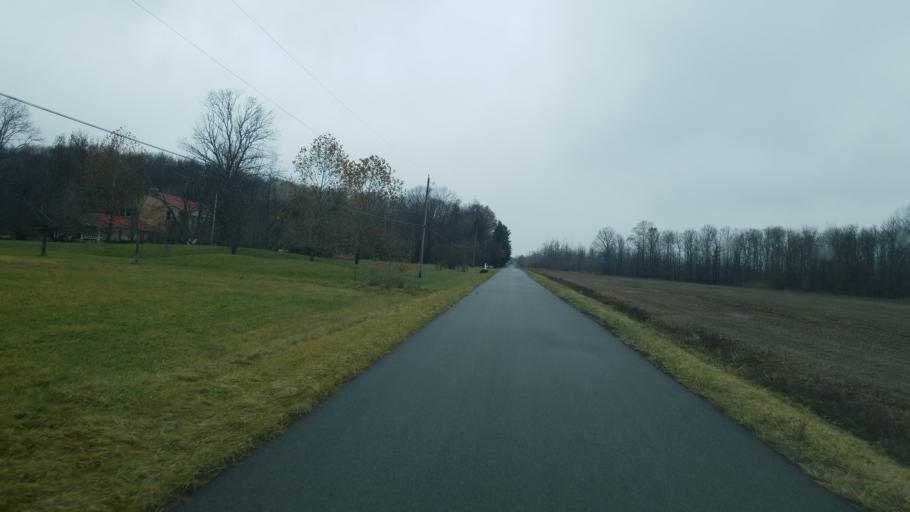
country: US
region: Ohio
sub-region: Ashtabula County
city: Andover
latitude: 41.5613
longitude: -80.7066
